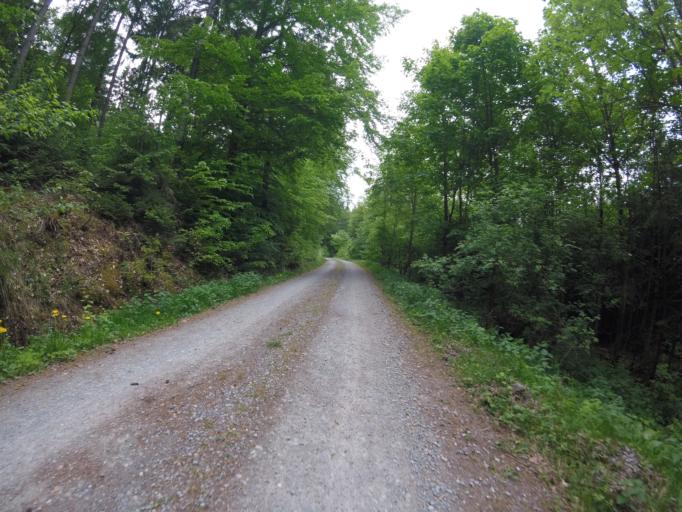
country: DE
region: Baden-Wuerttemberg
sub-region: Regierungsbezirk Stuttgart
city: Oppenweiler
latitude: 49.0104
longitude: 9.4464
